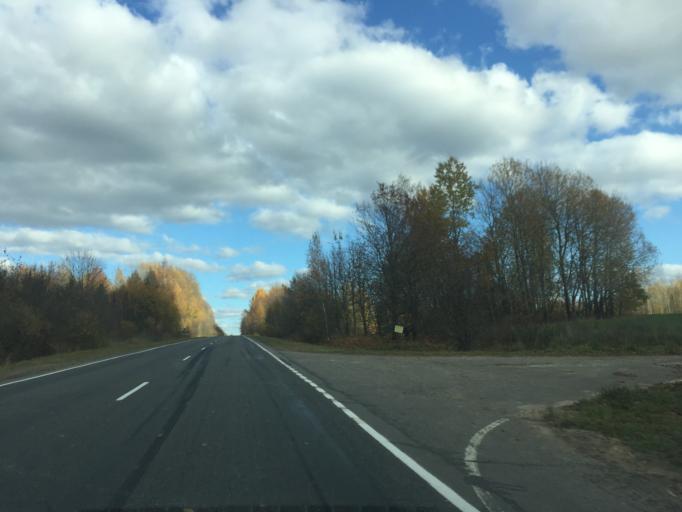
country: BY
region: Minsk
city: Narach
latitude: 54.9803
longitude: 26.7188
